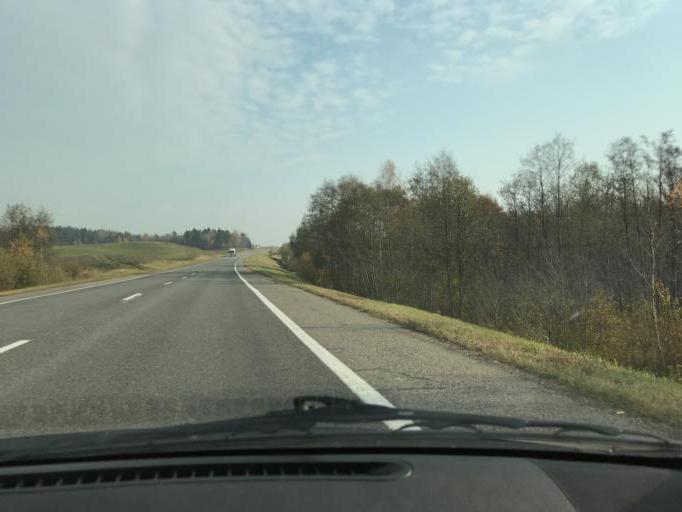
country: BY
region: Vitebsk
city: Lyepyel'
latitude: 54.9919
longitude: 28.9110
